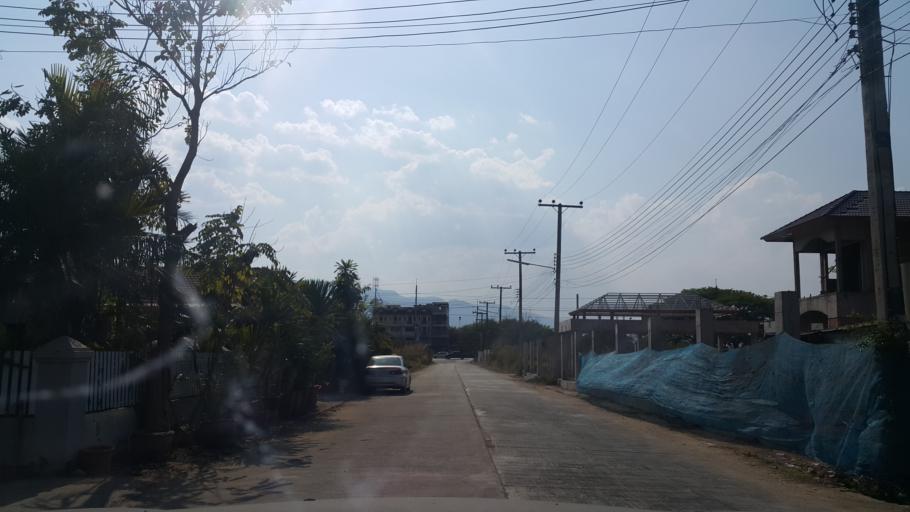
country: TH
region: Chiang Mai
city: San Sai
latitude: 18.8545
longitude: 99.0160
